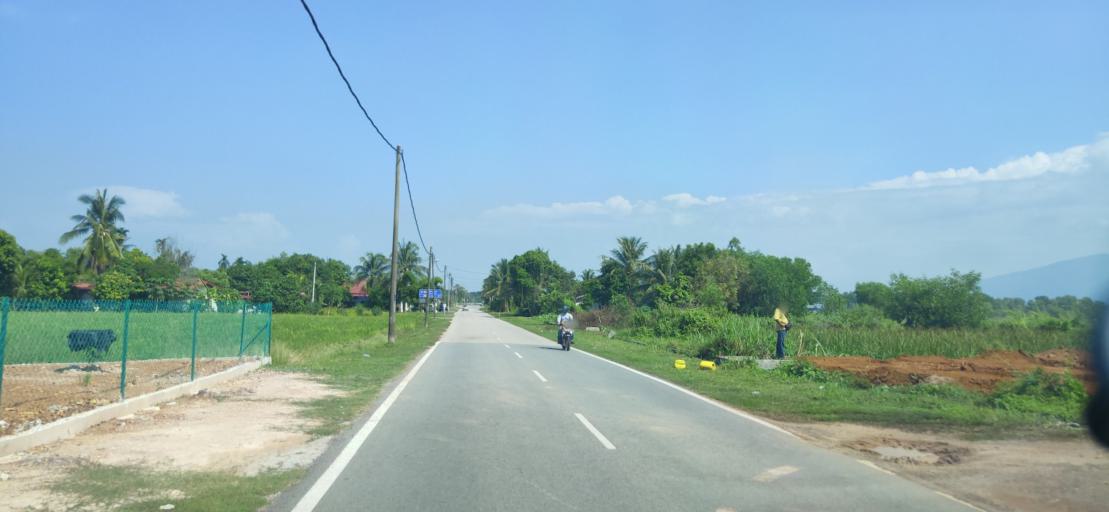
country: MY
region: Kedah
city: Sungai Petani
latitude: 5.6598
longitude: 100.4686
